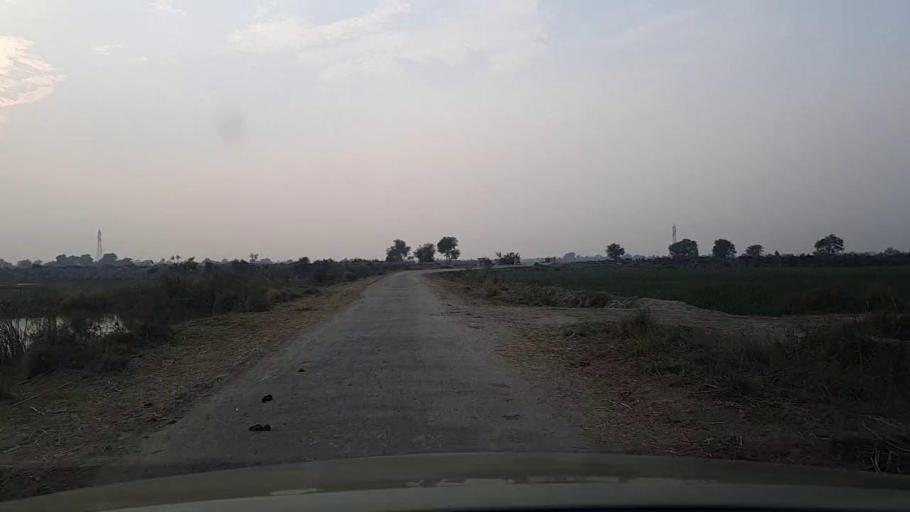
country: PK
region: Sindh
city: Sanghar
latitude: 26.1857
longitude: 68.9553
